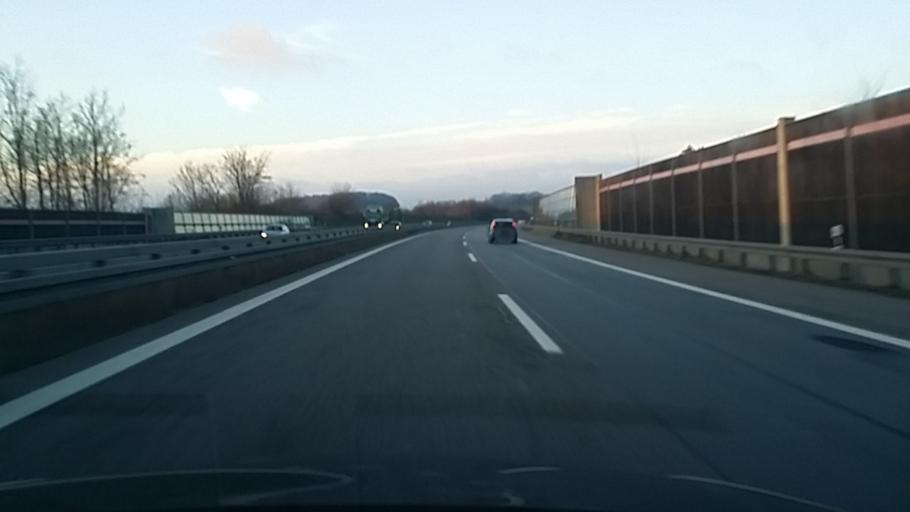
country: DE
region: Bavaria
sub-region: Upper Palatinate
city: Brunn
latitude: 49.0757
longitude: 11.9050
